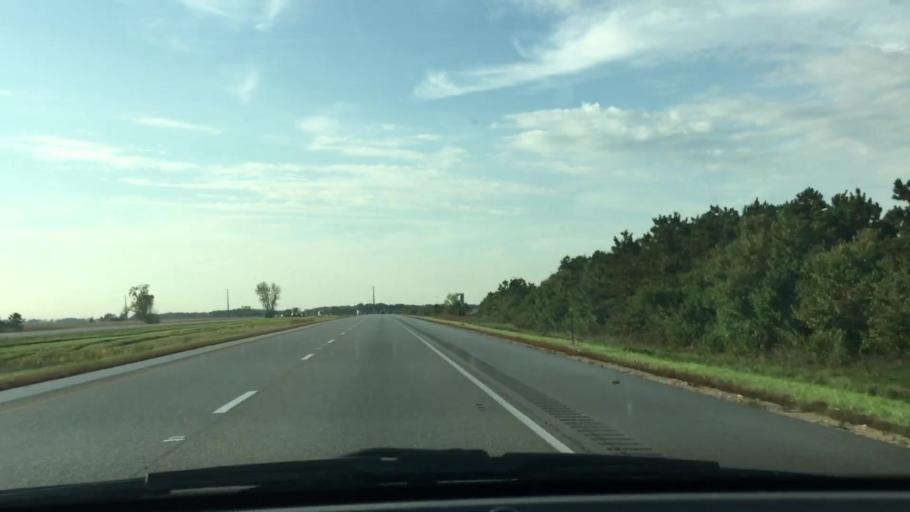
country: US
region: Illinois
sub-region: Ogle County
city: Davis Junction
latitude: 42.0772
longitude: -89.0217
